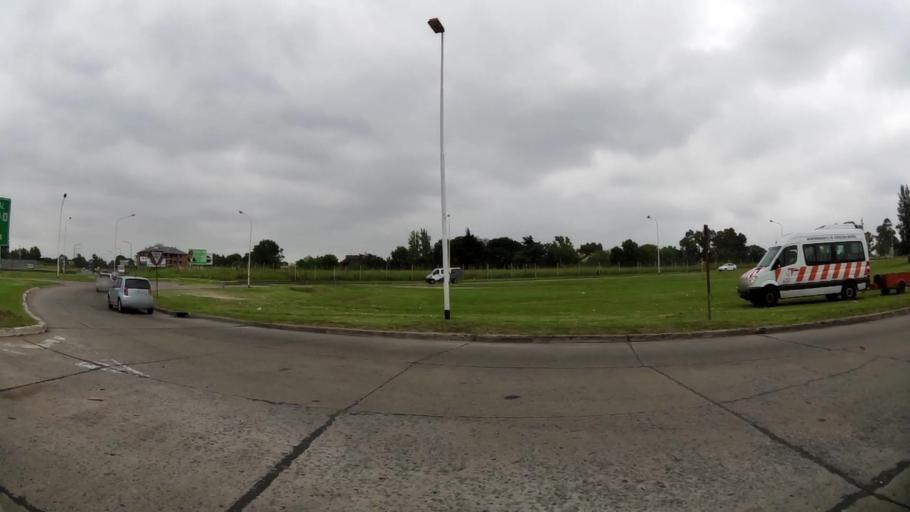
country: AR
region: Buenos Aires F.D.
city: Villa Lugano
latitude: -34.7272
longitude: -58.5164
